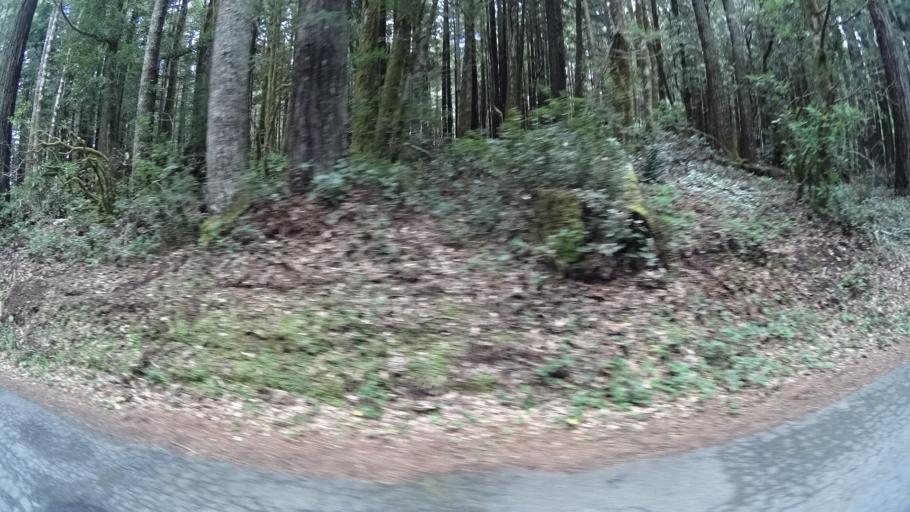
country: US
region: California
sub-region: Humboldt County
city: Blue Lake
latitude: 40.8103
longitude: -123.9913
